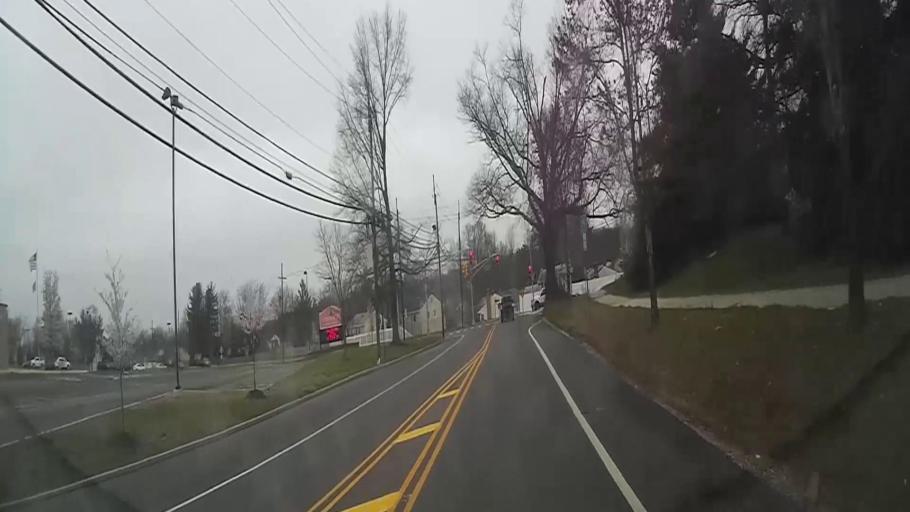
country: US
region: New Jersey
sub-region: Burlington County
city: Marlton
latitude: 39.8752
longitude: -74.8958
